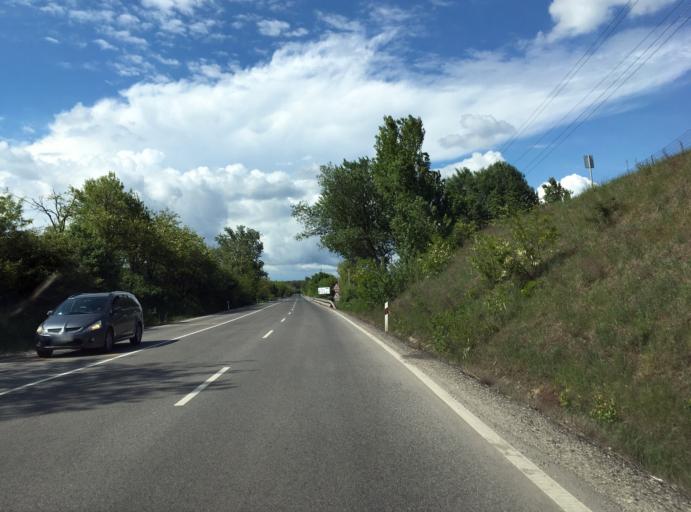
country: HU
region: Pest
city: Kerepes
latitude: 47.5698
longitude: 19.2929
